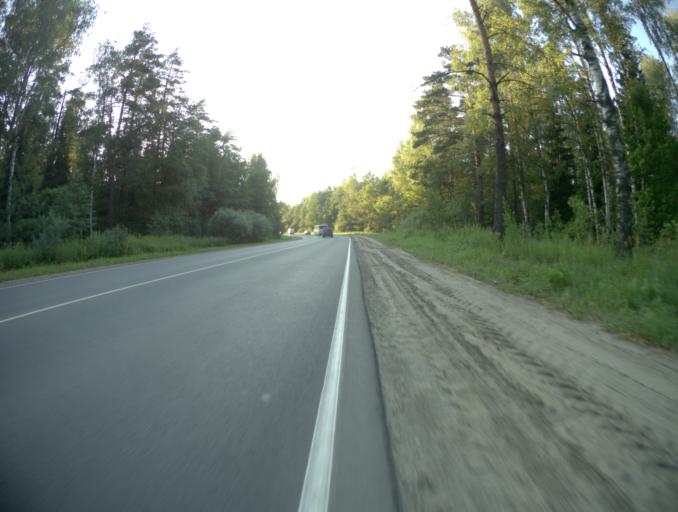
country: RU
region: Vladimir
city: Kommunar
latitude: 56.0591
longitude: 40.5157
